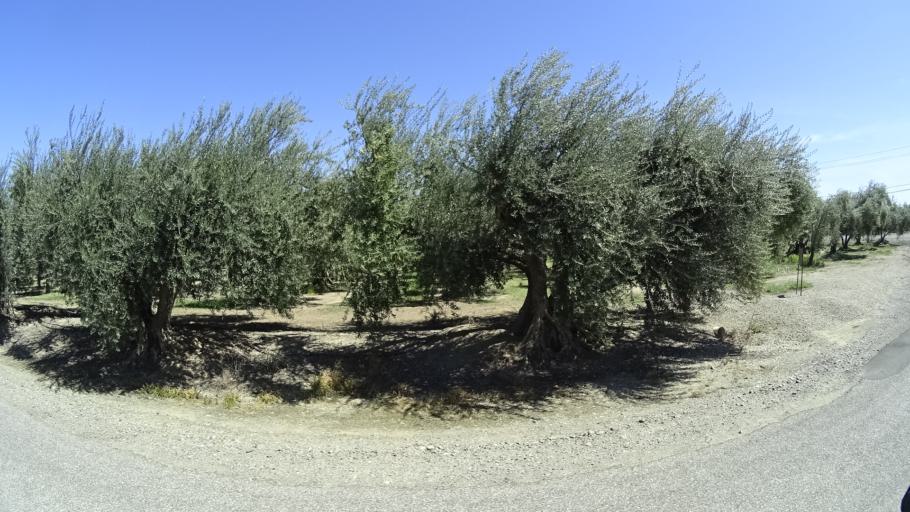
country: US
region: California
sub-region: Glenn County
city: Orland
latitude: 39.7476
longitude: -122.1504
